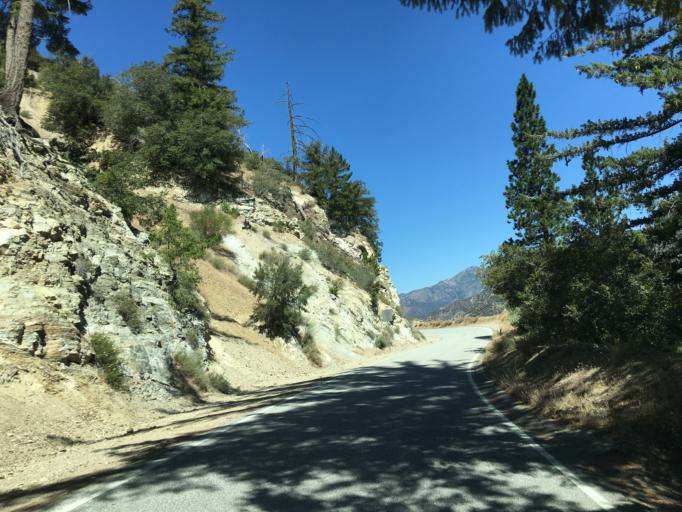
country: US
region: California
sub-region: San Bernardino County
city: San Antonio Heights
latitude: 34.2253
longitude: -117.6767
